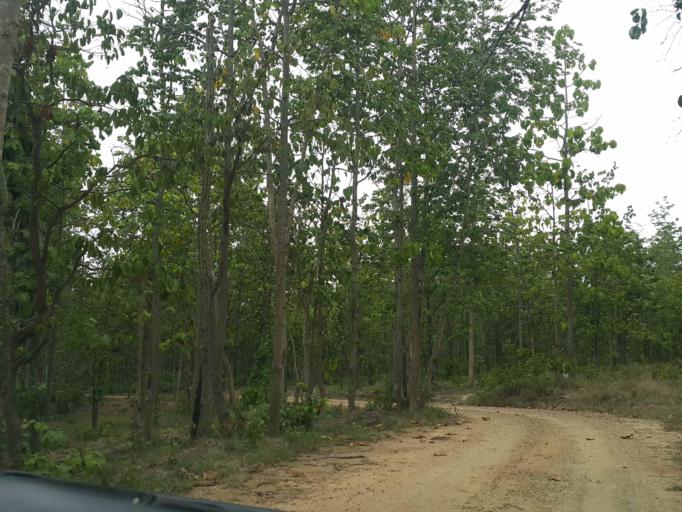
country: TH
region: Chiang Mai
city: Doi Lo
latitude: 18.5014
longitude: 98.7465
